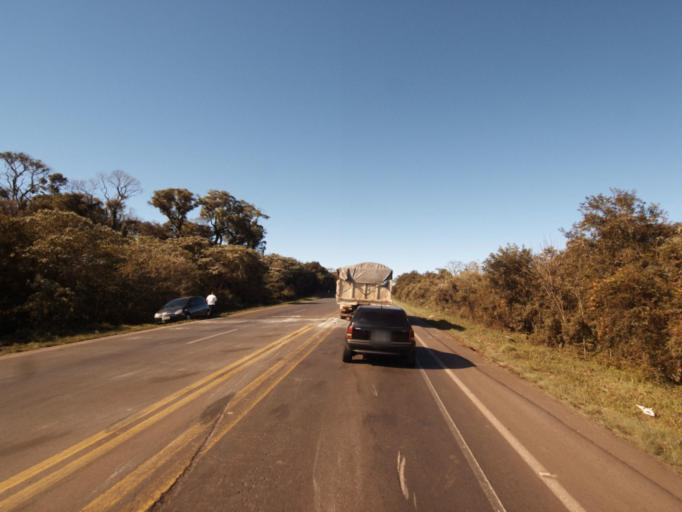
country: BR
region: Santa Catarina
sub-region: Xanxere
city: Xanxere
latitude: -26.9163
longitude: -52.4918
